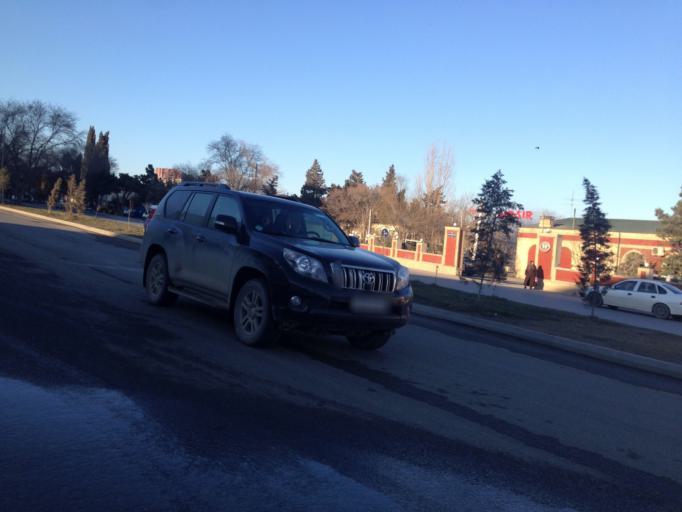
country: AZ
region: Baki
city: Binagadi
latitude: 40.4192
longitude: 49.8558
